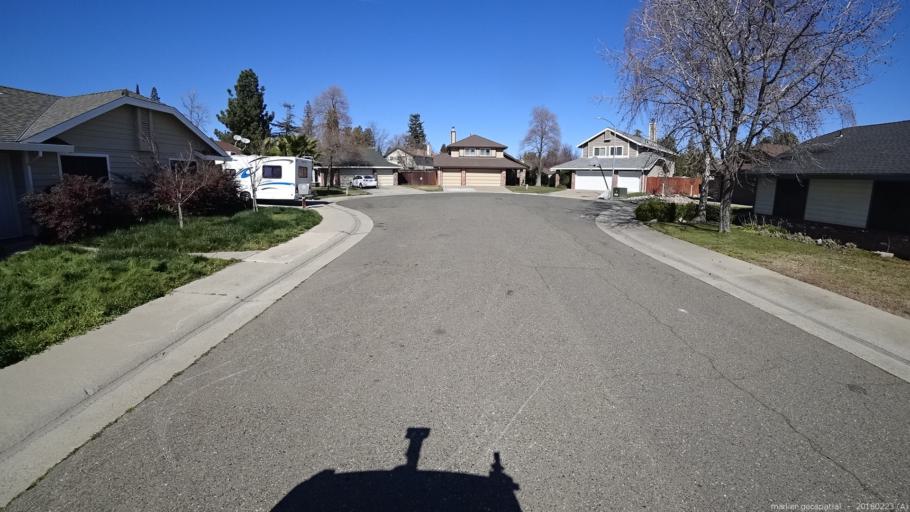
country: US
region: California
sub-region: Sacramento County
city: North Highlands
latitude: 38.7148
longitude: -121.3751
